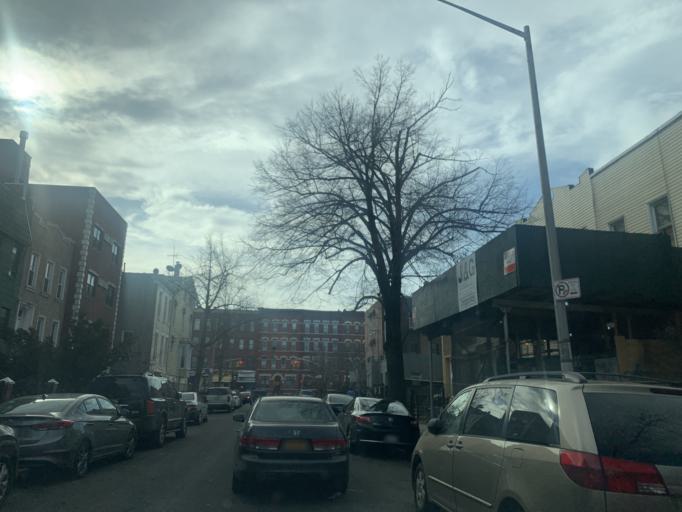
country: US
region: New York
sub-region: Kings County
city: Brooklyn
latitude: 40.6949
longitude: -73.9261
